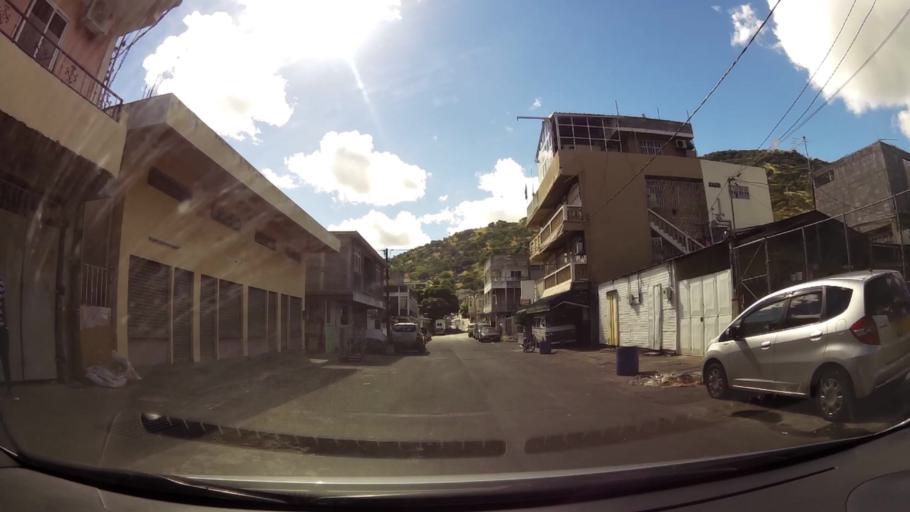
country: MU
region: Port Louis
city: Port Louis
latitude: -20.1639
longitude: 57.5174
